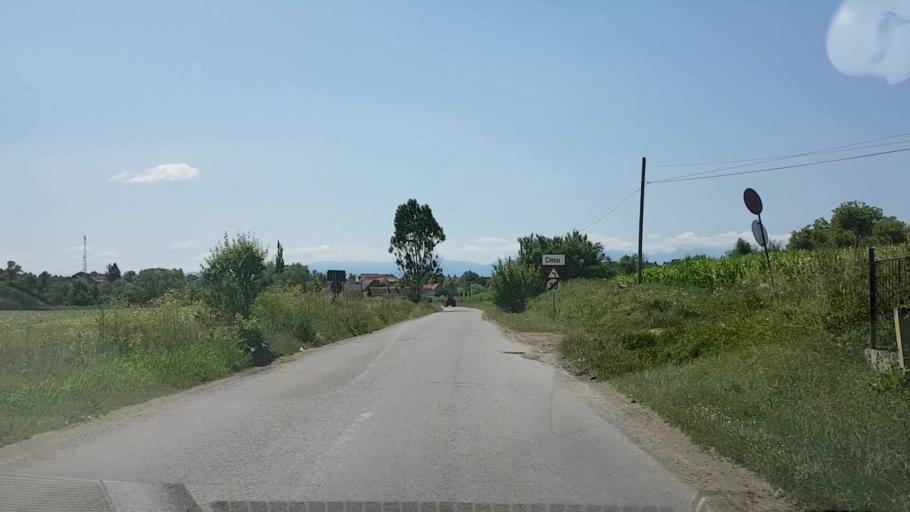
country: RO
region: Brasov
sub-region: Comuna Cincu
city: Cincu
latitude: 45.9220
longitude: 24.7982
